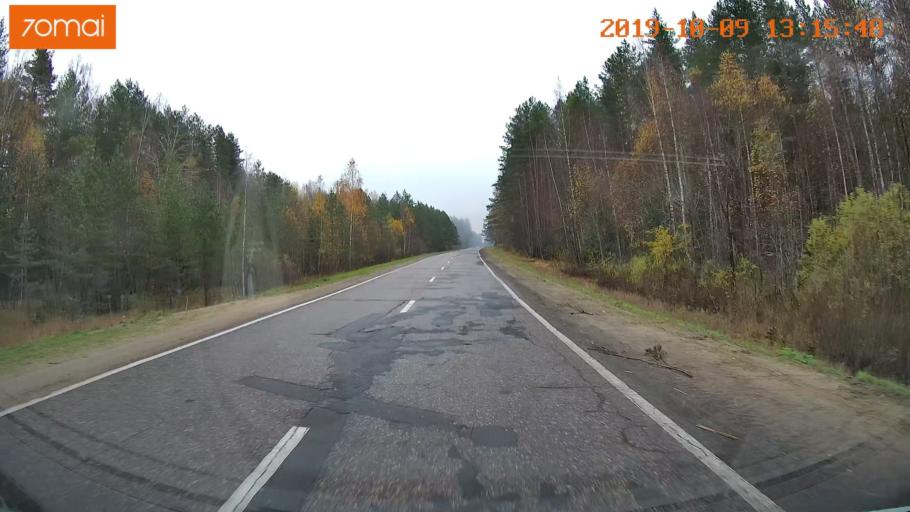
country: RU
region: Jaroslavl
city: Lyubim
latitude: 58.3655
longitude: 40.7573
